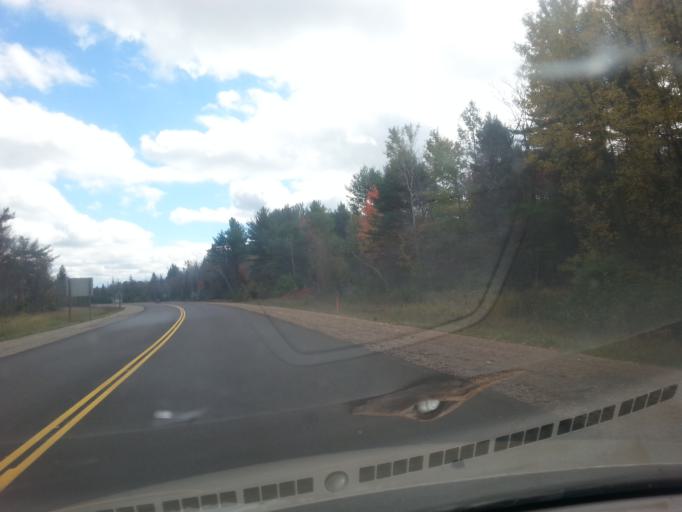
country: CA
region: Ontario
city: Pembroke
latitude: 45.7918
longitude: -77.1838
